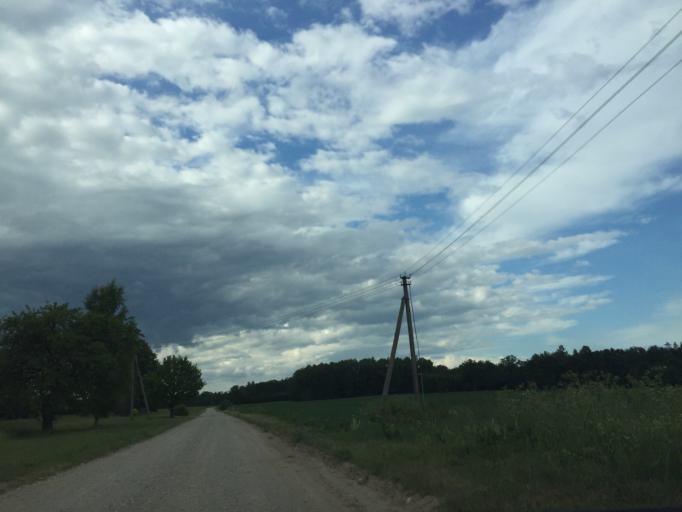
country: LV
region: Pargaujas
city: Stalbe
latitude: 57.3625
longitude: 24.9494
